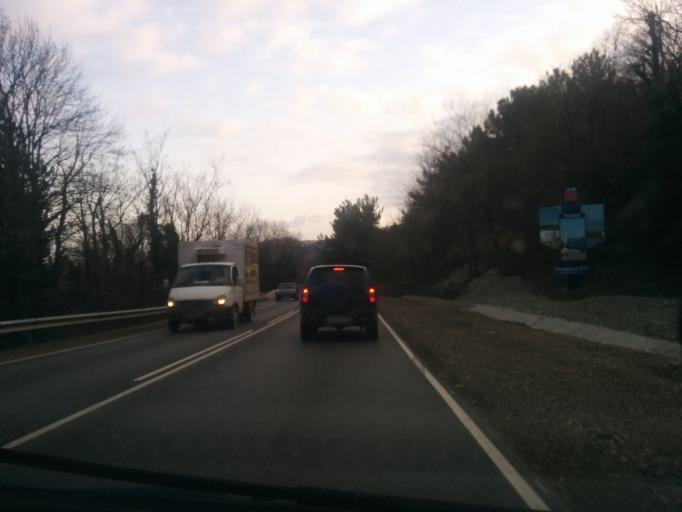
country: RU
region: Krasnodarskiy
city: Agoy
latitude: 44.1280
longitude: 39.0478
